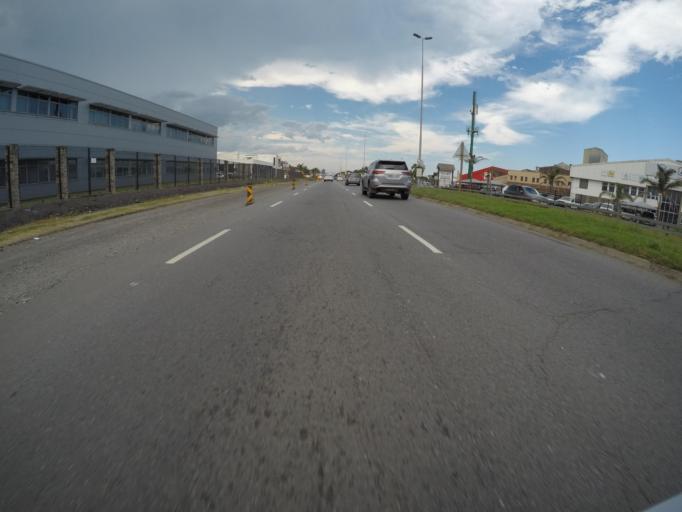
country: ZA
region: Eastern Cape
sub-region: Buffalo City Metropolitan Municipality
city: East London
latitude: -33.0302
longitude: 27.8863
